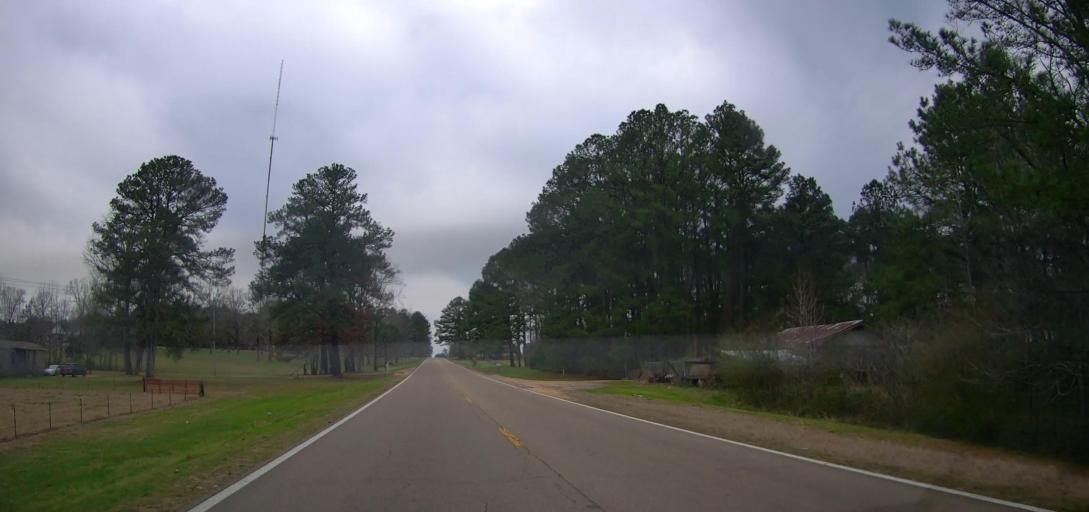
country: US
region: Mississippi
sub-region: Itawamba County
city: Mantachie
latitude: 34.2631
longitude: -88.5354
